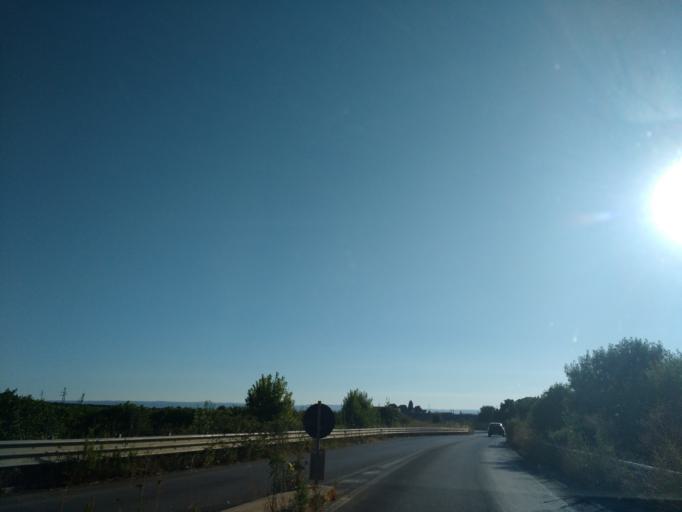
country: IT
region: Sicily
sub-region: Provincia di Siracusa
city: Belvedere
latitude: 37.0612
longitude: 15.2363
